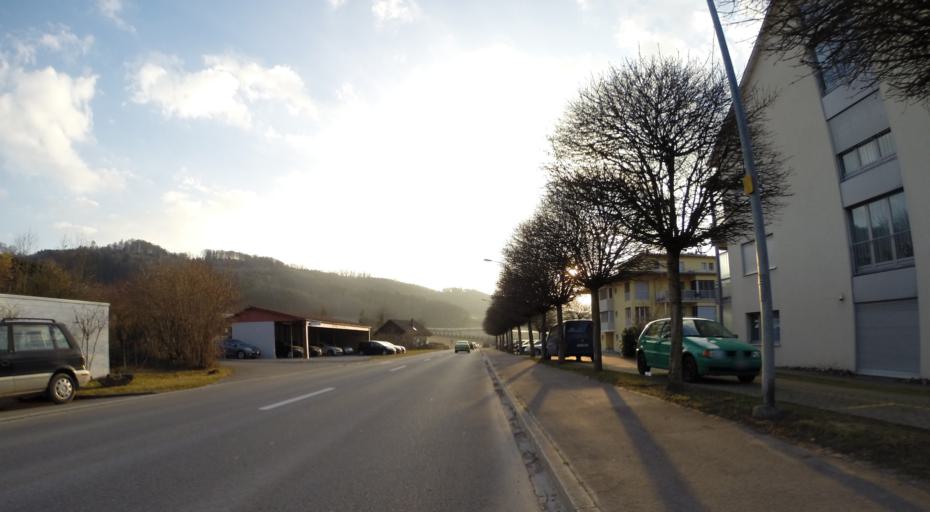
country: DE
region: Baden-Wuerttemberg
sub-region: Freiburg Region
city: Ohningen
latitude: 47.6444
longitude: 8.9120
